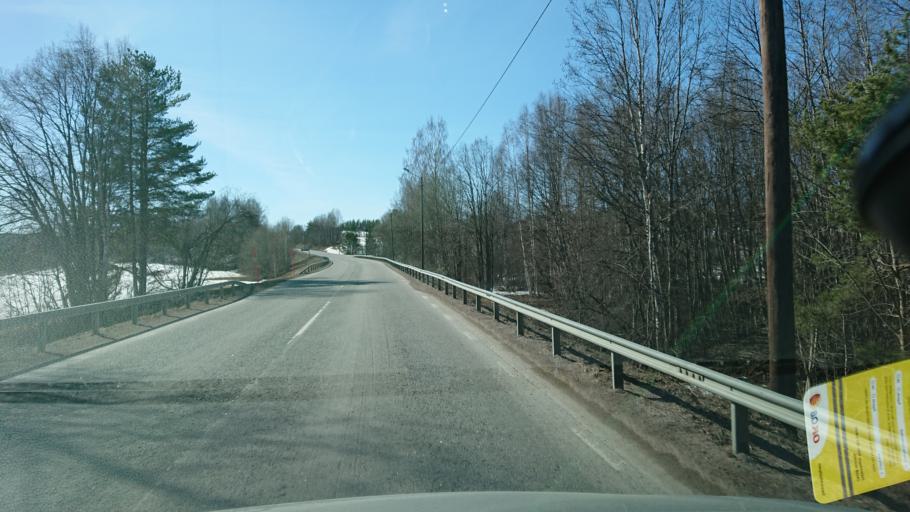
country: SE
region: Vaesternorrland
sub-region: Solleftea Kommun
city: As
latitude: 63.6496
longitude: 16.4604
